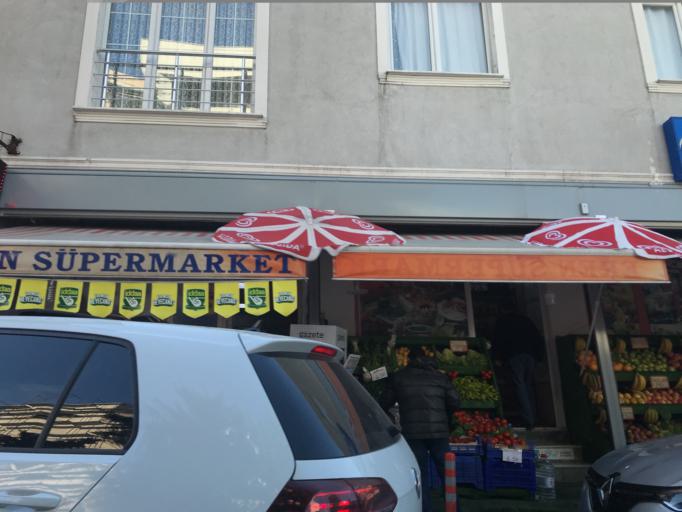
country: TR
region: Istanbul
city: Mahmutbey
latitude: 41.0328
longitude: 28.7746
